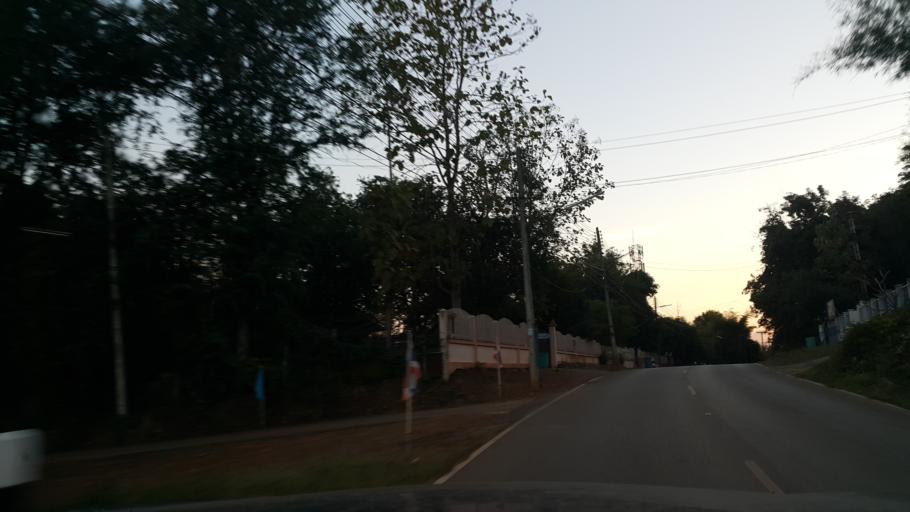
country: TH
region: Uttaradit
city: Uttaradit
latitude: 17.6575
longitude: 100.0931
